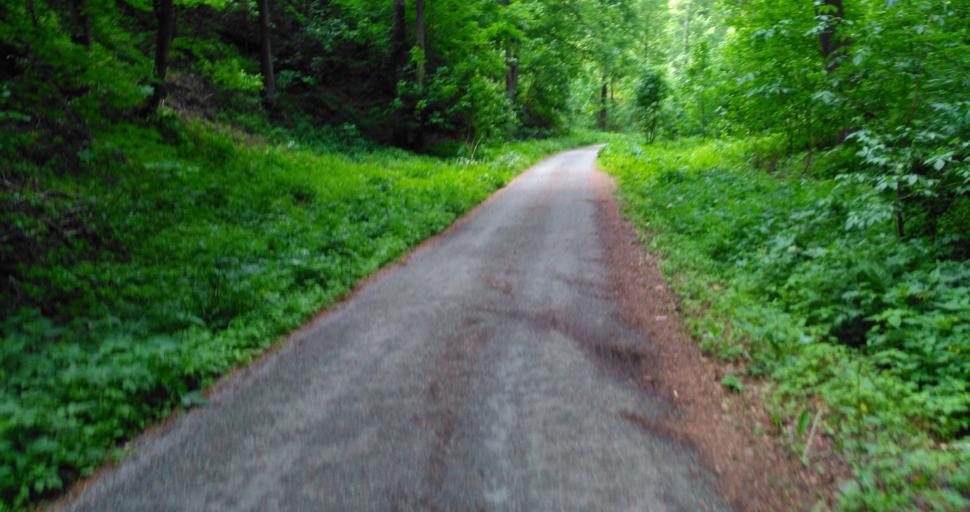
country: CZ
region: South Moravian
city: Ostrov u Macochy
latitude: 49.3869
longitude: 16.7302
